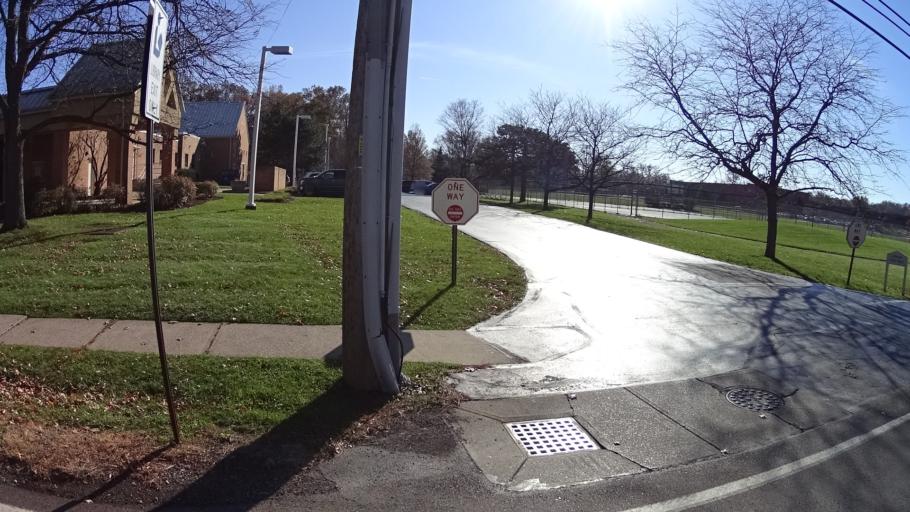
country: US
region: Ohio
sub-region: Lorain County
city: Avon Lake
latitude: 41.5103
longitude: -82.0136
